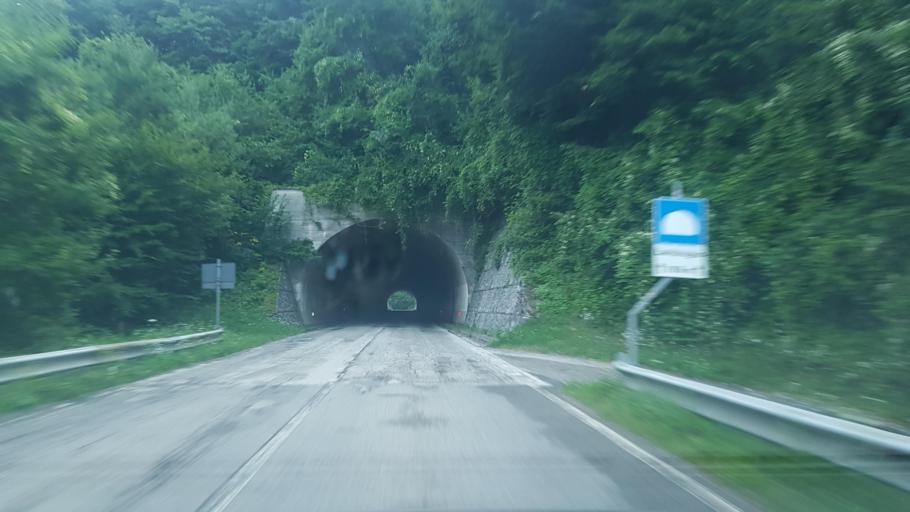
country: IT
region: Friuli Venezia Giulia
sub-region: Provincia di Udine
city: Paularo
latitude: 46.5017
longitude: 13.1123
